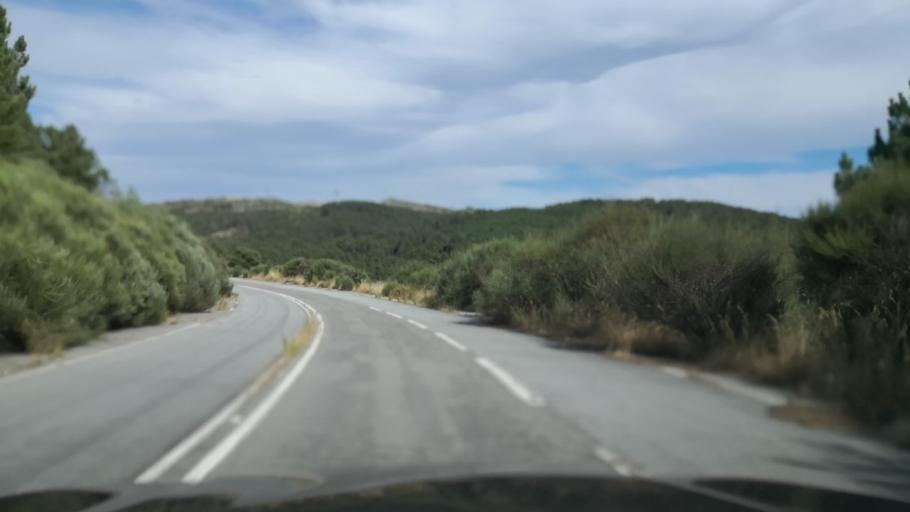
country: PT
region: Vila Real
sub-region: Sabrosa
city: Sabrosa
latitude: 41.3560
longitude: -7.5855
